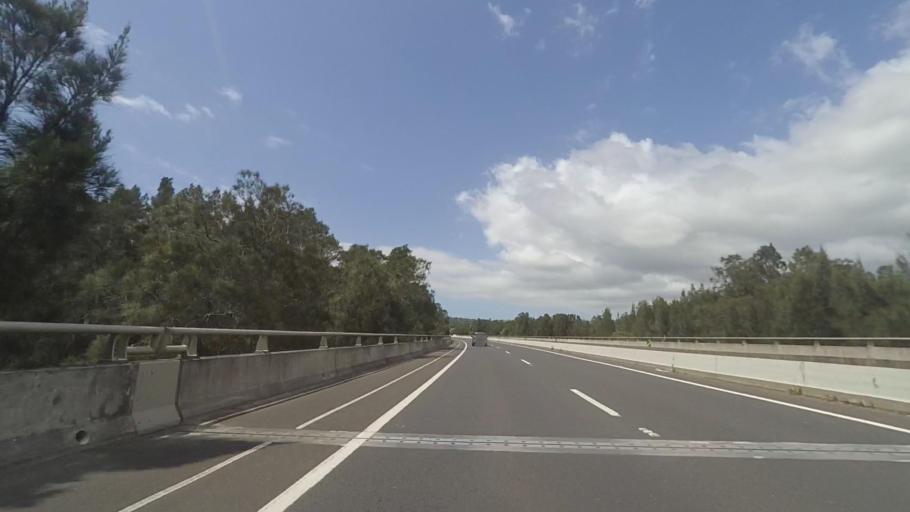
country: AU
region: New South Wales
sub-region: Kiama
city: Kiama
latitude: -34.6374
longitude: 150.8322
